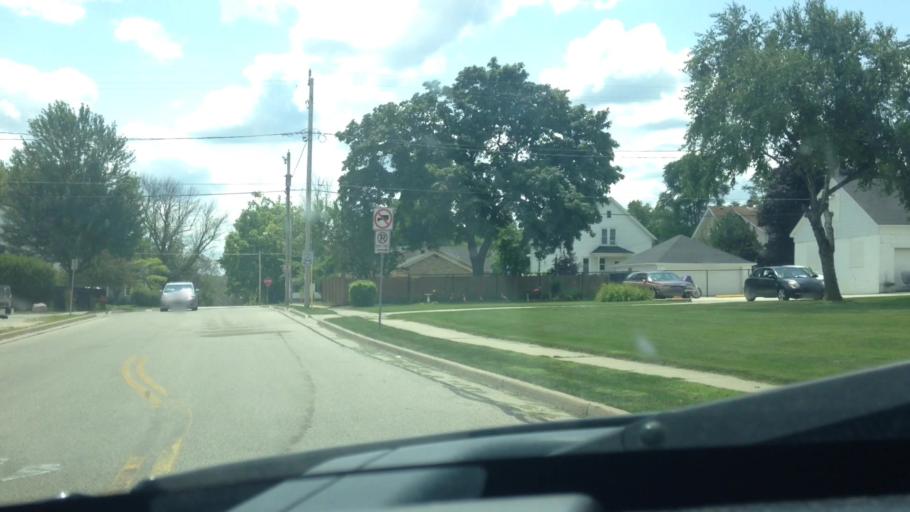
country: US
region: Wisconsin
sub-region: Waukesha County
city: Menomonee Falls
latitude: 43.1793
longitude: -88.1089
